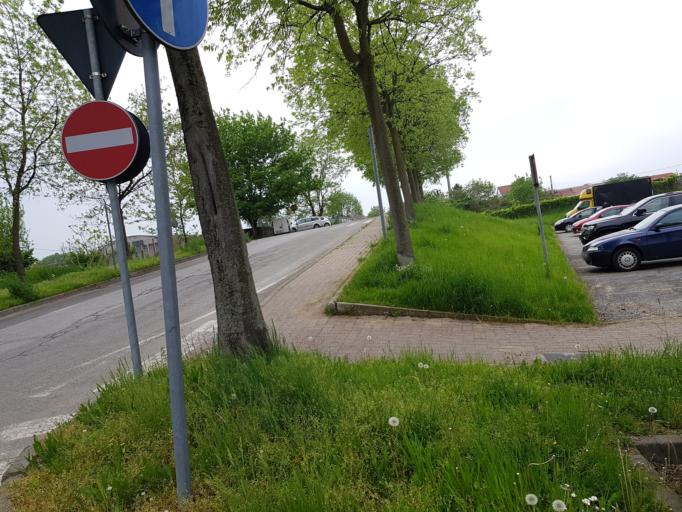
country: IT
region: Piedmont
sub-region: Provincia di Torino
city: Lesna
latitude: 45.0572
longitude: 7.6109
